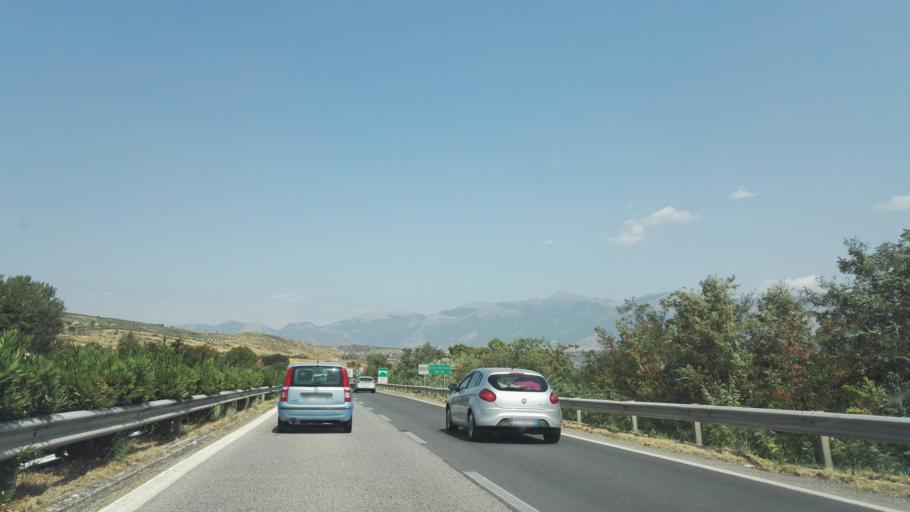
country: IT
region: Calabria
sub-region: Provincia di Cosenza
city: Firmo
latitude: 39.7307
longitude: 16.2343
